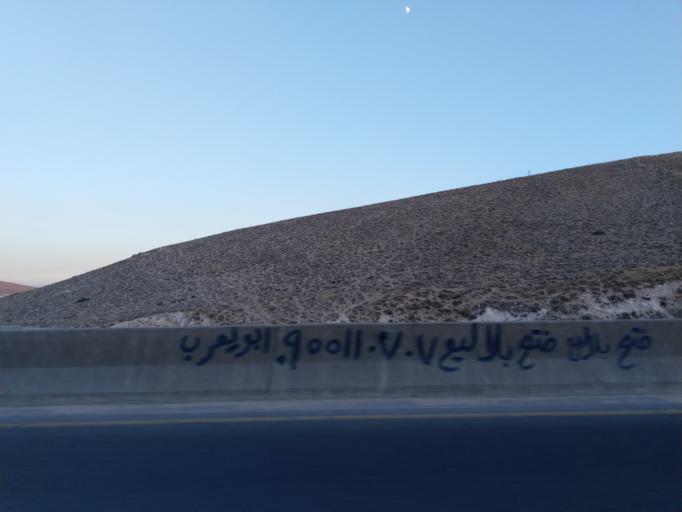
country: SY
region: Rif-dimashq
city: At Tall
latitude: 33.5843
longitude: 36.2889
